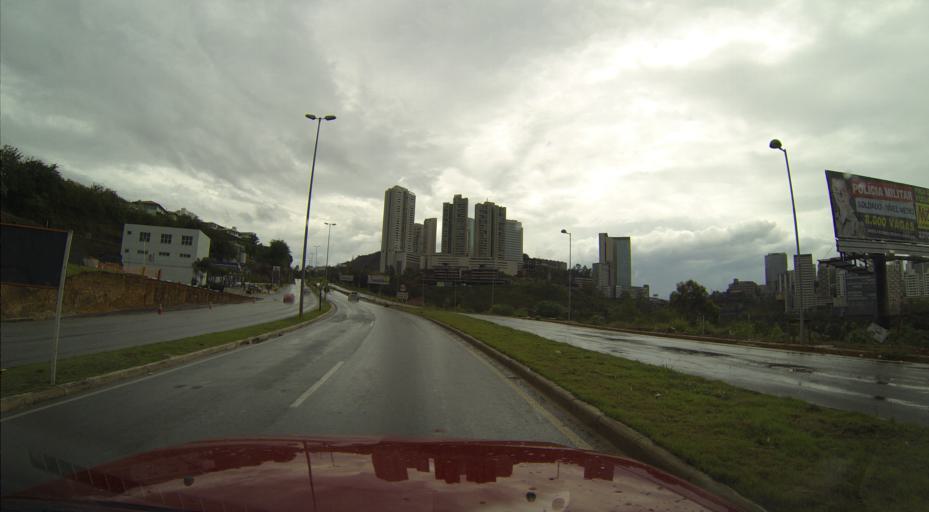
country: BR
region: Minas Gerais
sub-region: Belo Horizonte
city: Belo Horizonte
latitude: -19.9867
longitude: -43.9402
